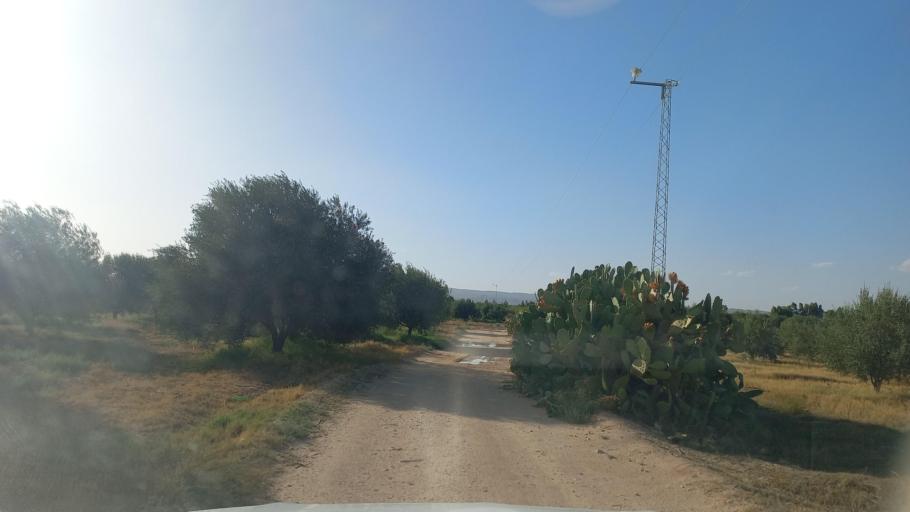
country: TN
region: Al Qasrayn
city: Kasserine
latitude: 35.2614
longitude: 9.0283
